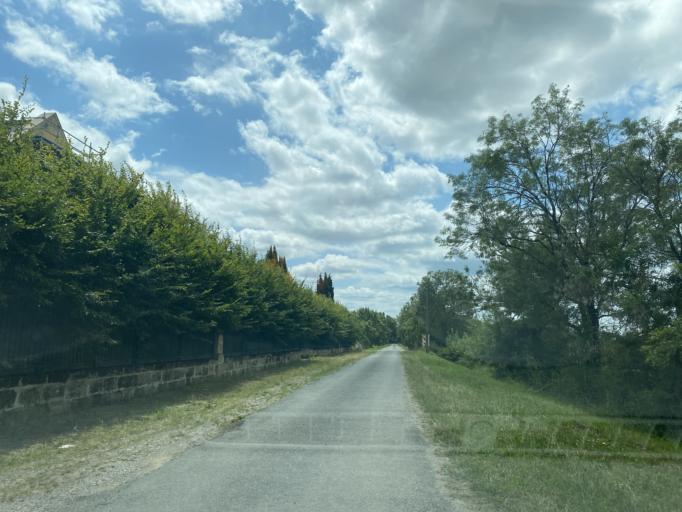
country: FR
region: Aquitaine
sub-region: Departement de la Gironde
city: Margaux
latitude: 45.0679
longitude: -0.6678
